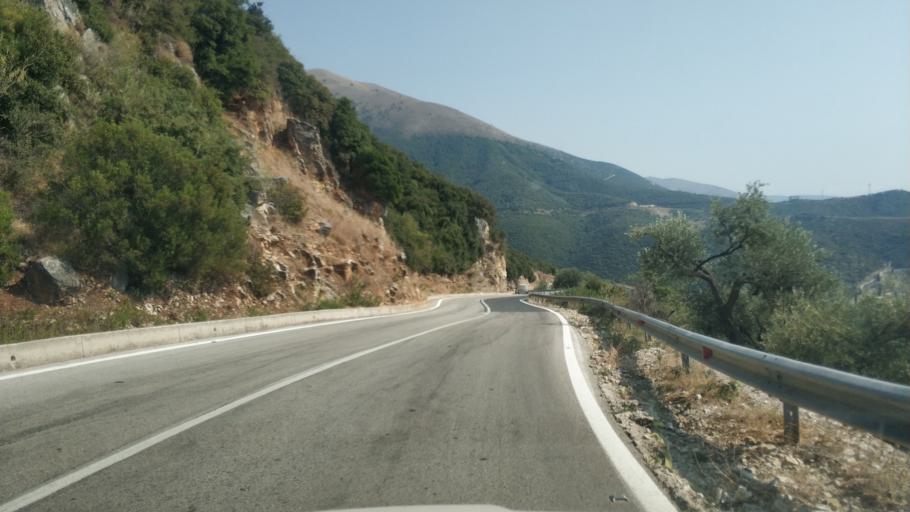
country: AL
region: Vlore
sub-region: Rrethi i Sarandes
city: Lukove
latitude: 40.0149
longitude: 19.8972
